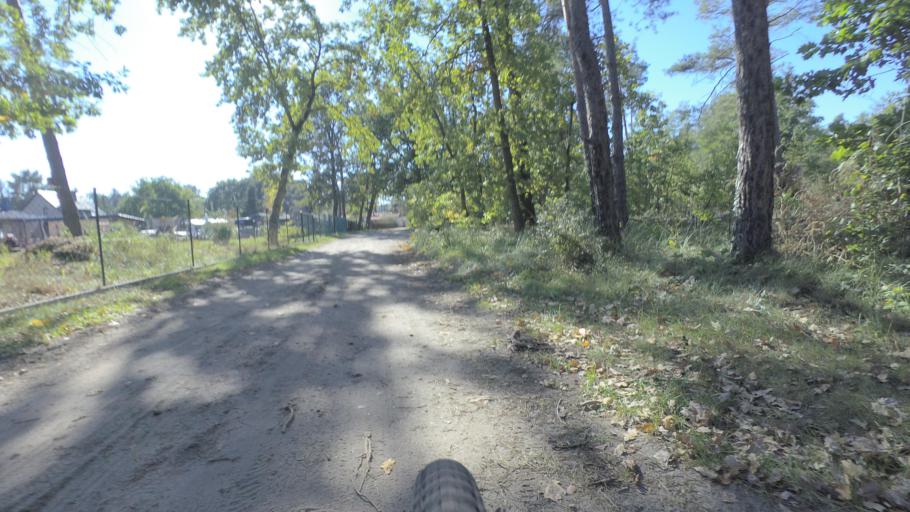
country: DE
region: Brandenburg
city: Am Mellensee
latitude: 52.1701
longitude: 13.3908
